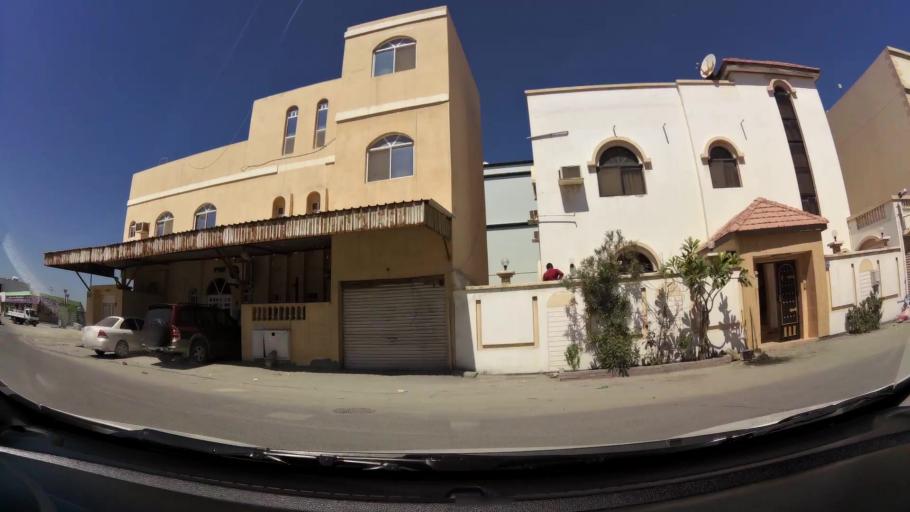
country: BH
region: Muharraq
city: Al Muharraq
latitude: 26.2867
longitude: 50.6269
